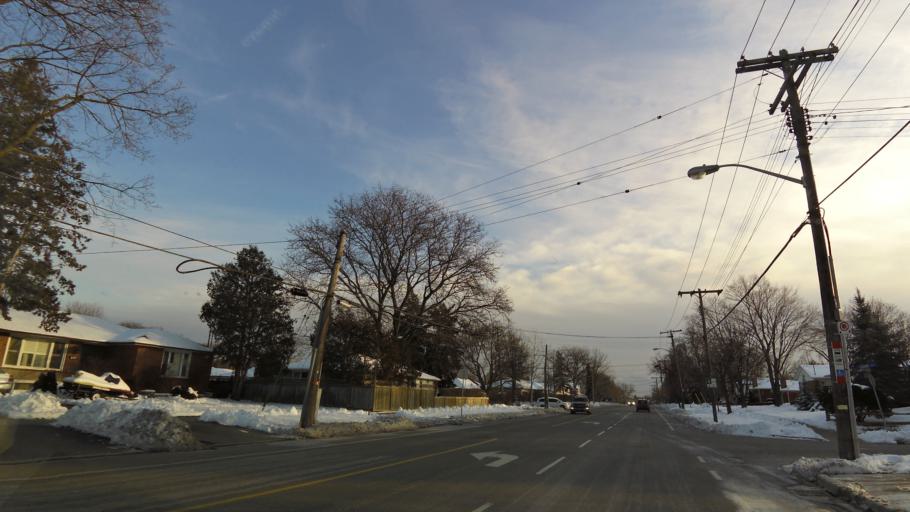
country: CA
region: Ontario
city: Etobicoke
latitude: 43.6670
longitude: -79.5598
